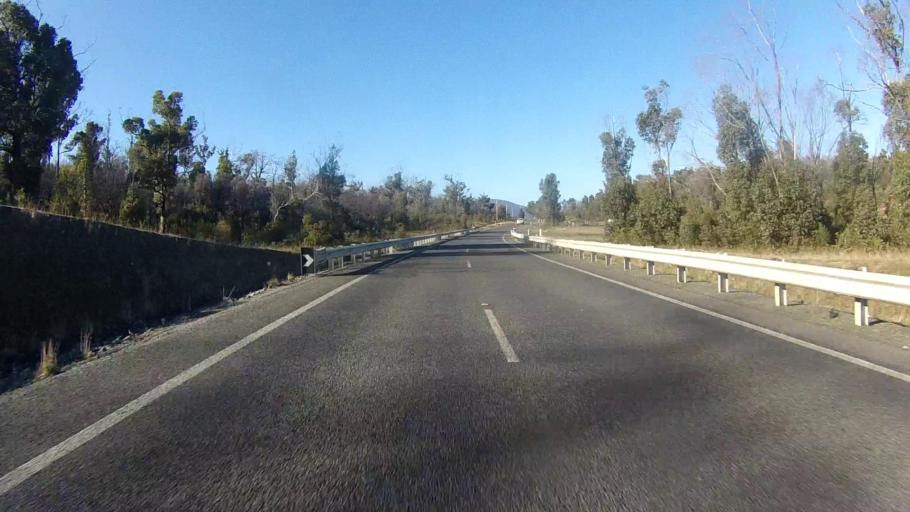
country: AU
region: Tasmania
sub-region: Sorell
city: Sorell
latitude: -42.9282
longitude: 147.8424
